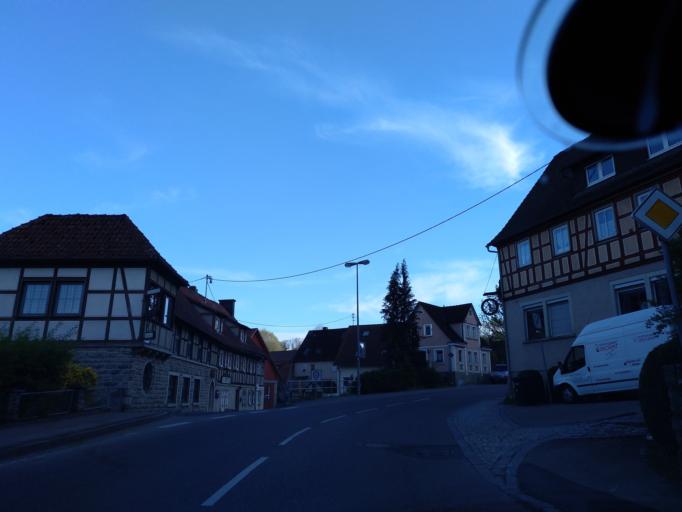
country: DE
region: Baden-Wuerttemberg
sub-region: Regierungsbezirk Stuttgart
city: Kirchberg an der Jagst
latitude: 49.2058
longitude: 9.9847
